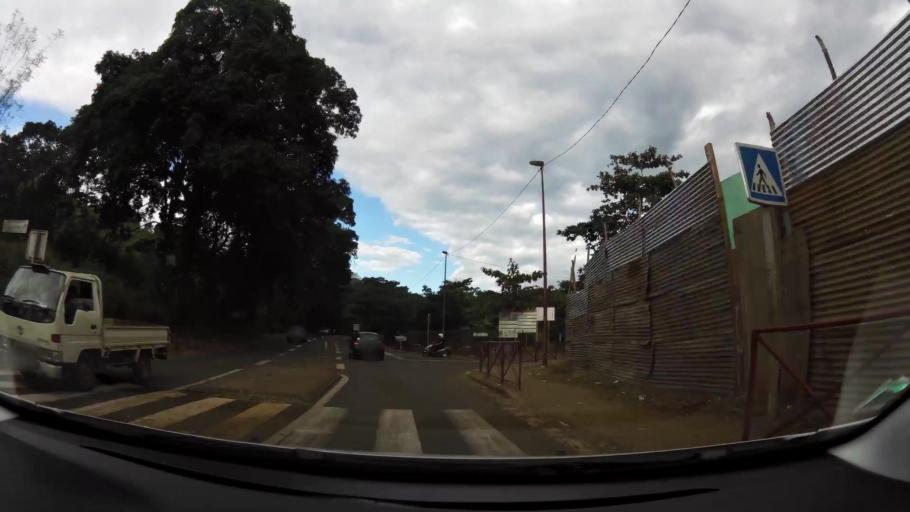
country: YT
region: Dembeni
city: Dembeni
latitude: -12.8385
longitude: 45.1698
